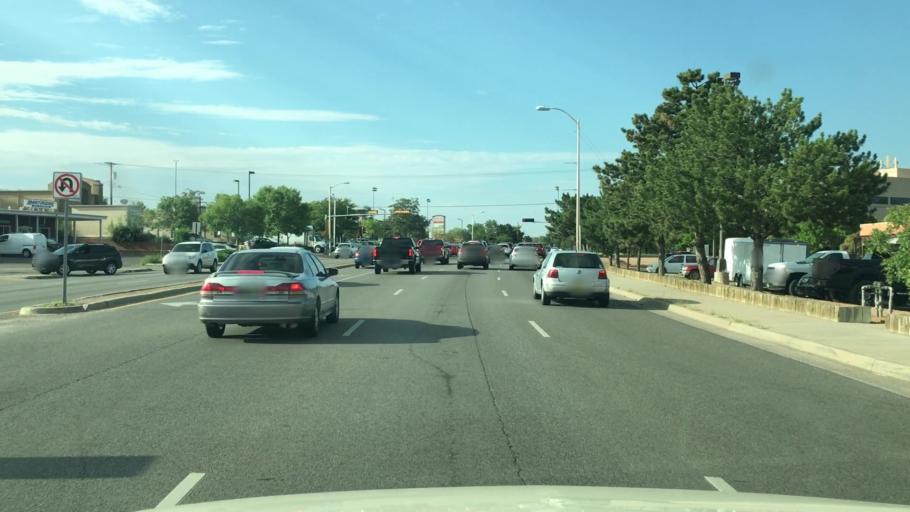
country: US
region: New Mexico
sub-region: Santa Fe County
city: Santa Fe
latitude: 35.6752
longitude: -105.9536
